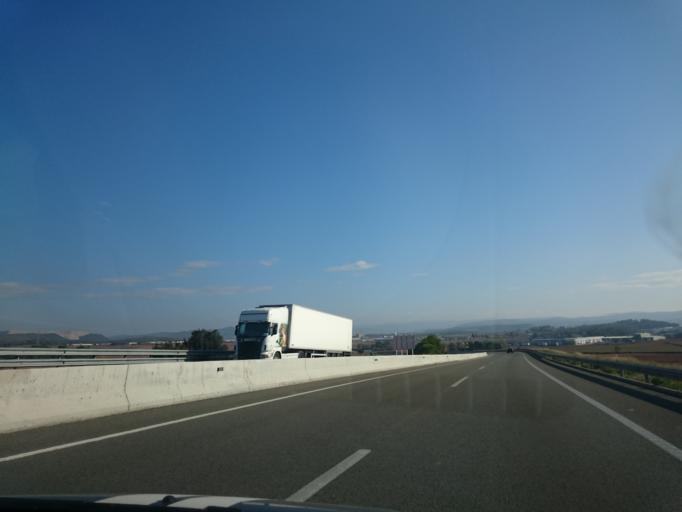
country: ES
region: Catalonia
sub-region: Provincia de Barcelona
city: Sant Fruitos de Bages
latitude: 41.7547
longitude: 1.8498
